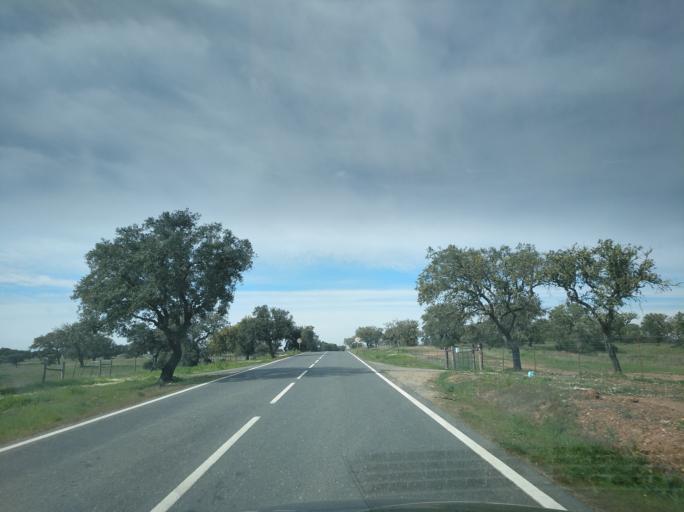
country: PT
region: Beja
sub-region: Mertola
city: Mertola
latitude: 37.7478
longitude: -7.7992
